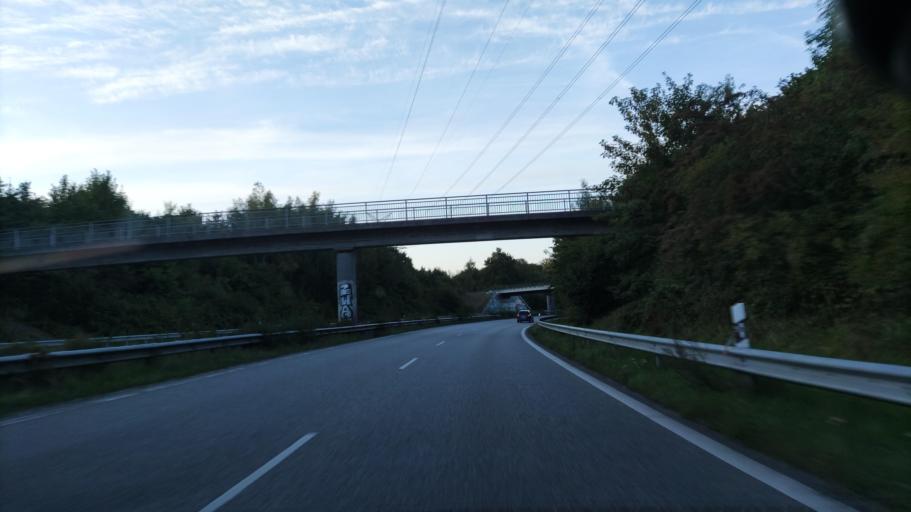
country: DE
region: Schleswig-Holstein
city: Monkeberg
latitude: 54.3366
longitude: 10.2051
